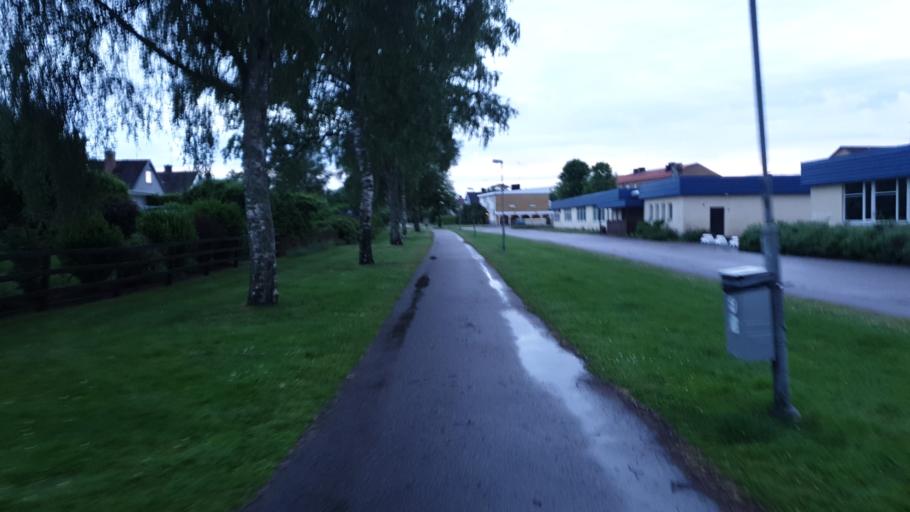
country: SE
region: Kronoberg
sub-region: Ljungby Kommun
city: Ljungby
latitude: 56.8303
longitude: 13.9564
